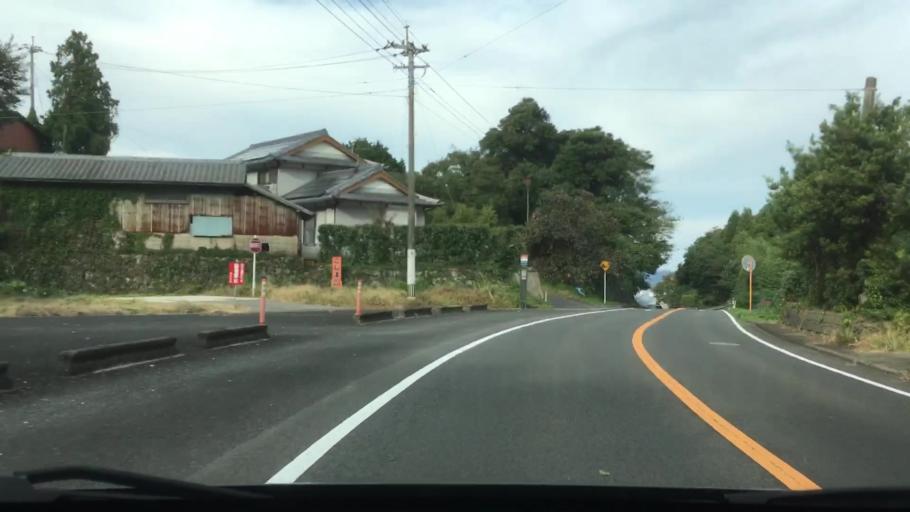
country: JP
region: Nagasaki
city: Sasebo
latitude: 33.0386
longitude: 129.6742
